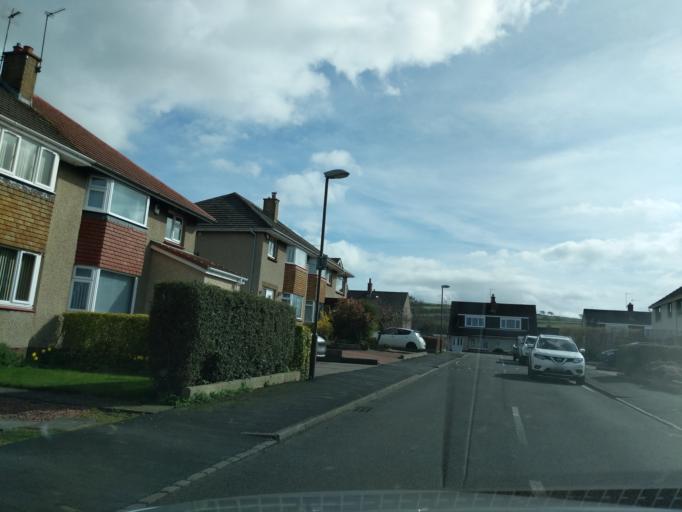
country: GB
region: Scotland
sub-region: Edinburgh
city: Currie
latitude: 55.9034
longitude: -3.3003
